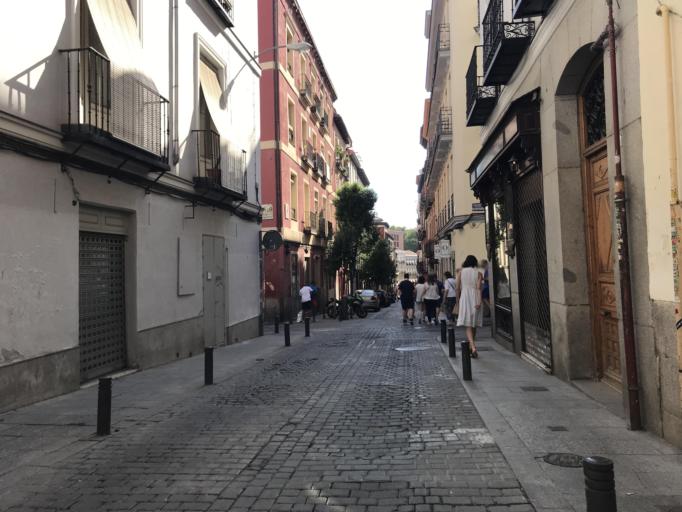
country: ES
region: Madrid
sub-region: Provincia de Madrid
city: Madrid
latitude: 40.4123
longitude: -3.6971
